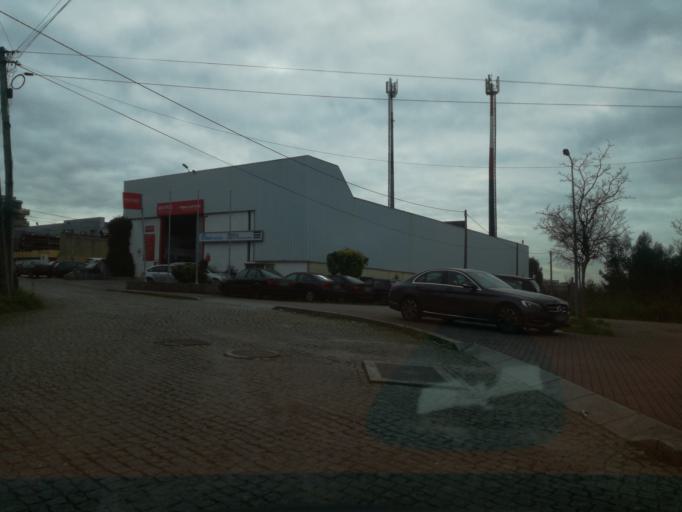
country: PT
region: Porto
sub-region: Maia
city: Anta
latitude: 41.2699
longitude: -8.6128
